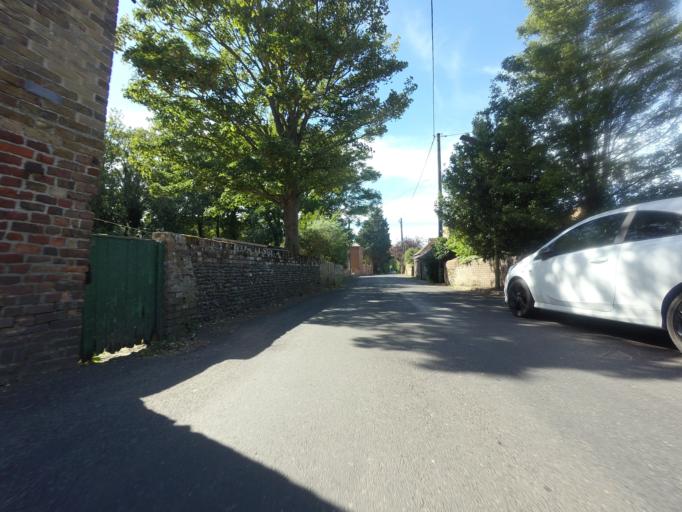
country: GB
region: England
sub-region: Kent
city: Birchington-on-Sea
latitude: 51.3542
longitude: 1.2507
